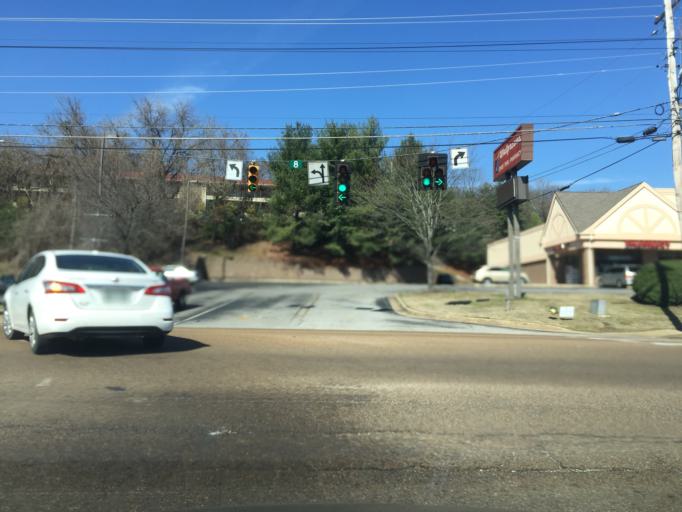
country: US
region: Tennessee
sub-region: Hamilton County
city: Red Bank
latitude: 35.1216
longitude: -85.2878
